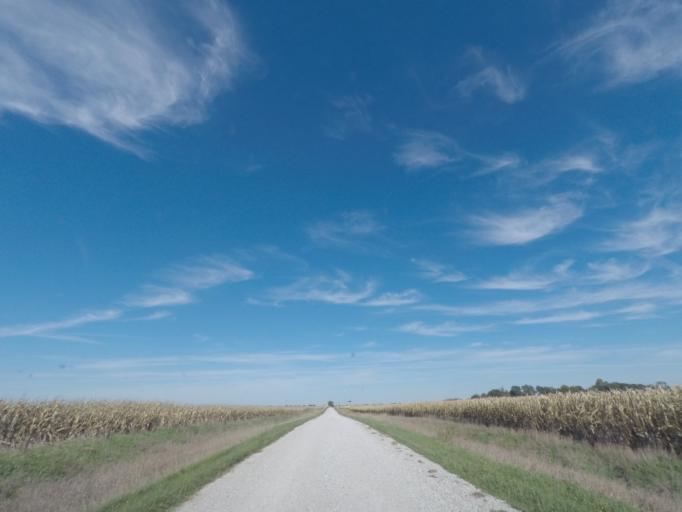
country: US
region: Iowa
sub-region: Story County
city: Nevada
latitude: 42.0158
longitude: -93.3573
